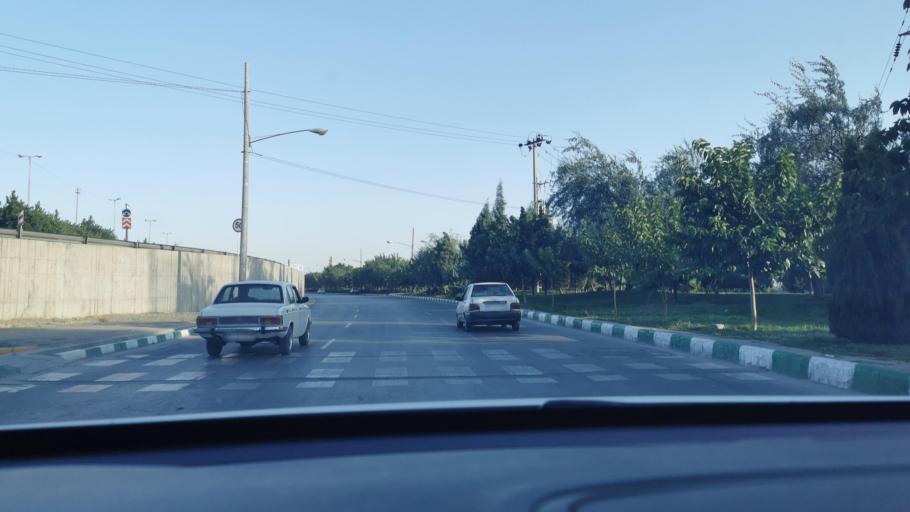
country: IR
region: Razavi Khorasan
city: Mashhad
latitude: 36.2781
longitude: 59.6552
